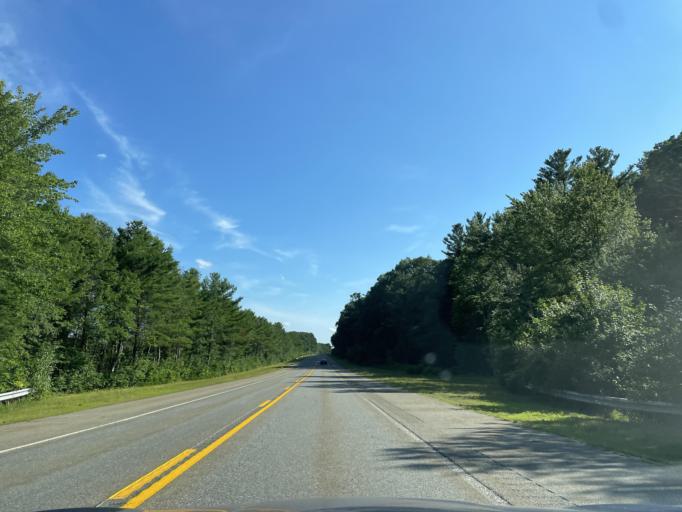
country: US
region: Massachusetts
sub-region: Worcester County
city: Sturbridge
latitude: 42.1603
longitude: -72.0343
